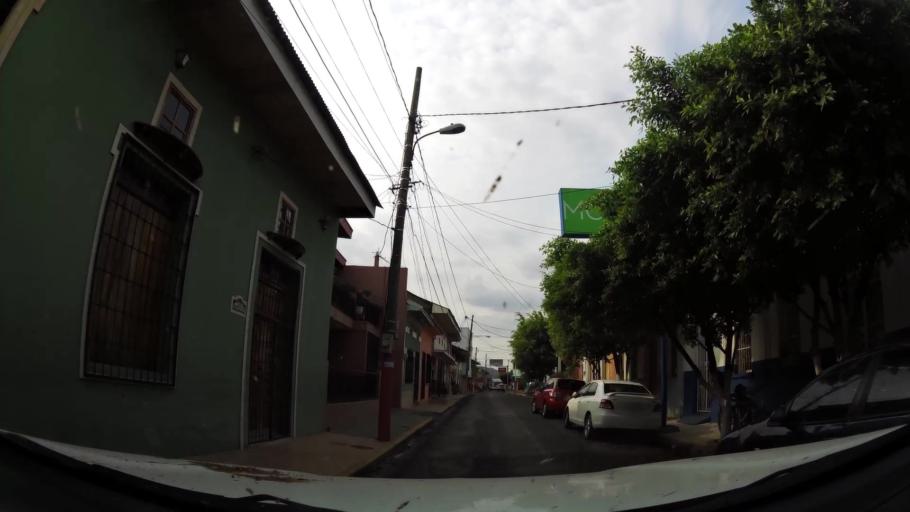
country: NI
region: Masaya
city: Masaya
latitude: 11.9715
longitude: -86.0940
